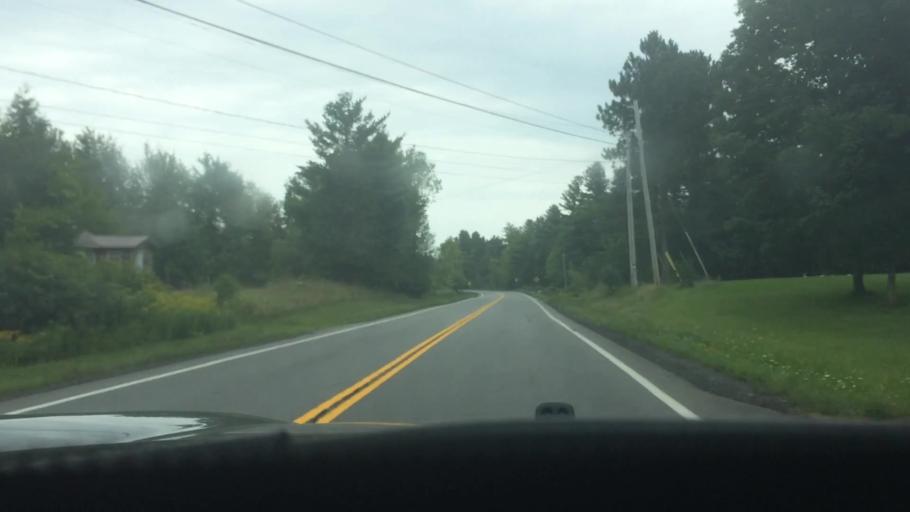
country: US
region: New York
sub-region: St. Lawrence County
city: Hannawa Falls
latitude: 44.6311
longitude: -74.8013
